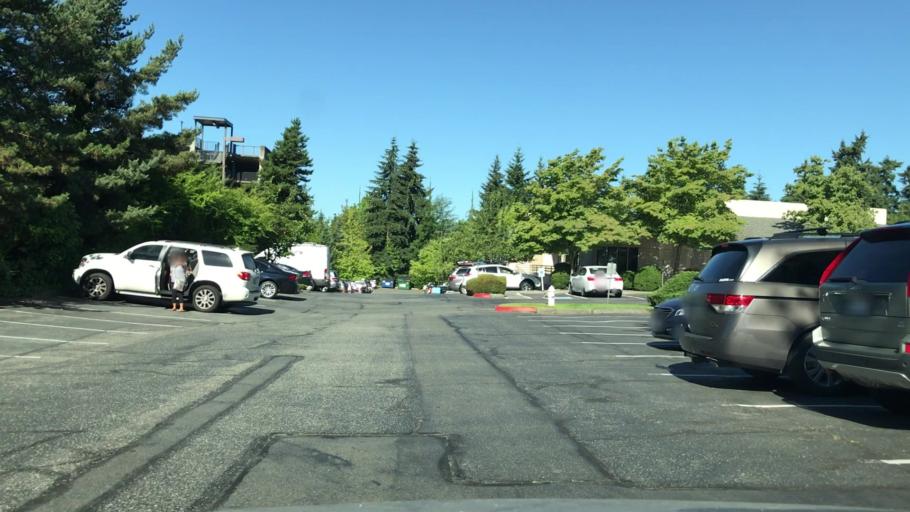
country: US
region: Washington
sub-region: King County
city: Kingsgate
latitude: 47.7159
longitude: -122.1818
